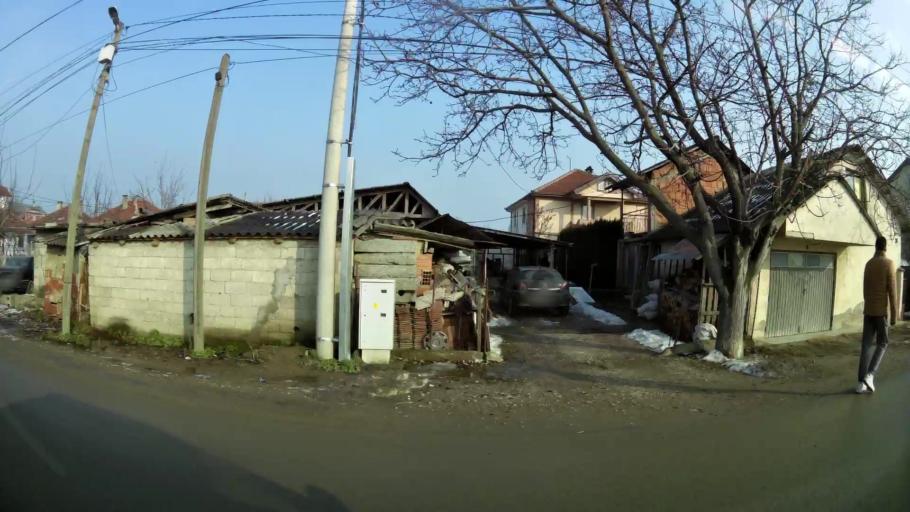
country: MK
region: Ilinden
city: Marino
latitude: 41.9800
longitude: 21.5929
